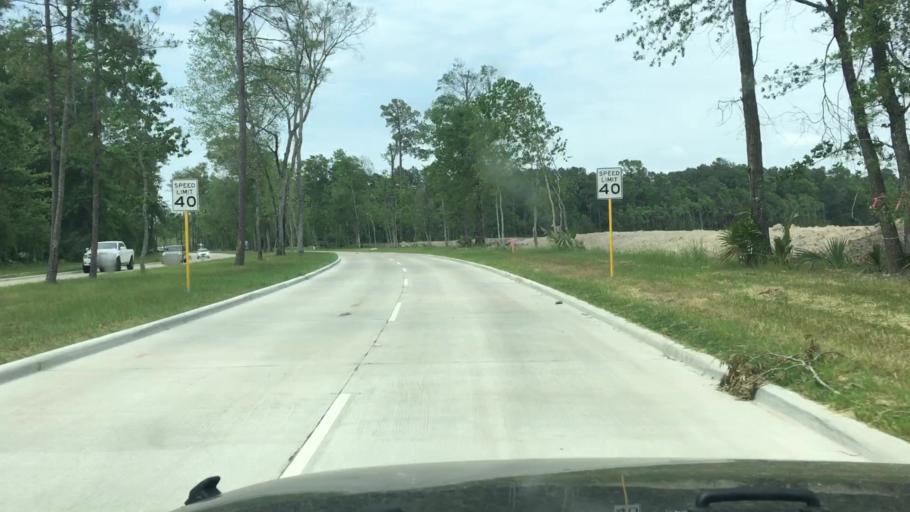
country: US
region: Texas
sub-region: Harris County
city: Atascocita
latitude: 29.9519
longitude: -95.2104
